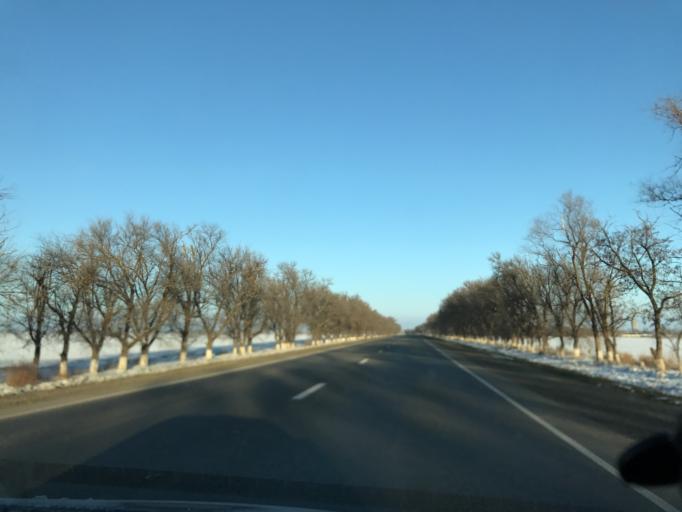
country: RU
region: Stavropol'skiy
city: Bezopasnoye
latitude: 45.6214
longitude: 41.9363
